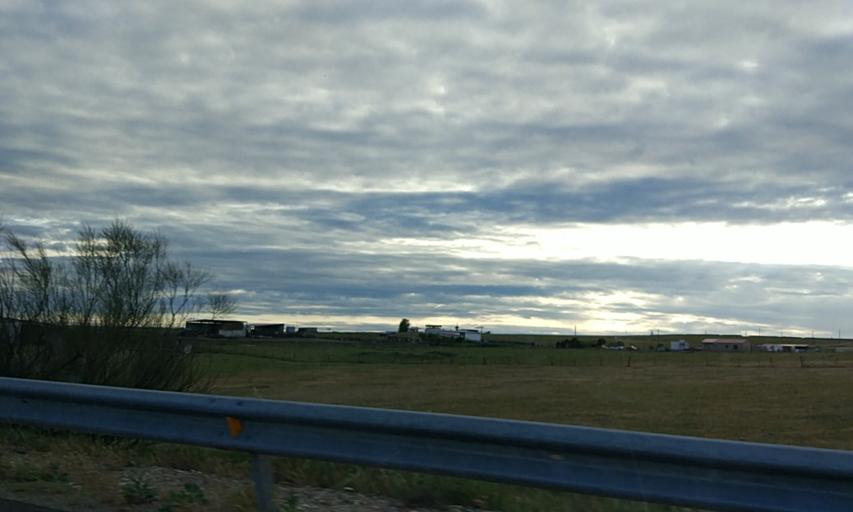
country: ES
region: Extremadura
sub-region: Provincia de Caceres
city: Casar de Caceres
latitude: 39.5495
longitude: -6.4036
